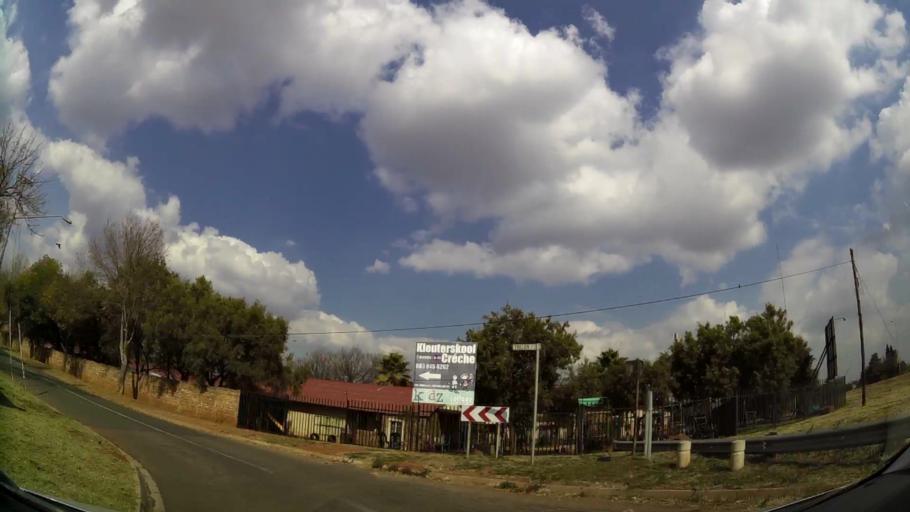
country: ZA
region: Gauteng
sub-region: City of Tshwane Metropolitan Municipality
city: Centurion
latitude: -25.8317
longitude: 28.2556
